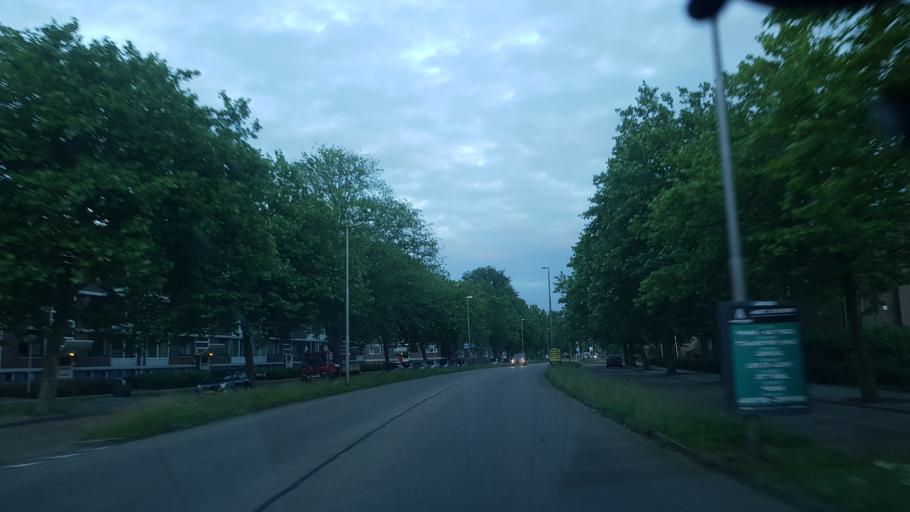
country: NL
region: Friesland
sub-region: Gemeente Leeuwarden
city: Leeuwarden
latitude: 53.2116
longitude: 5.8149
